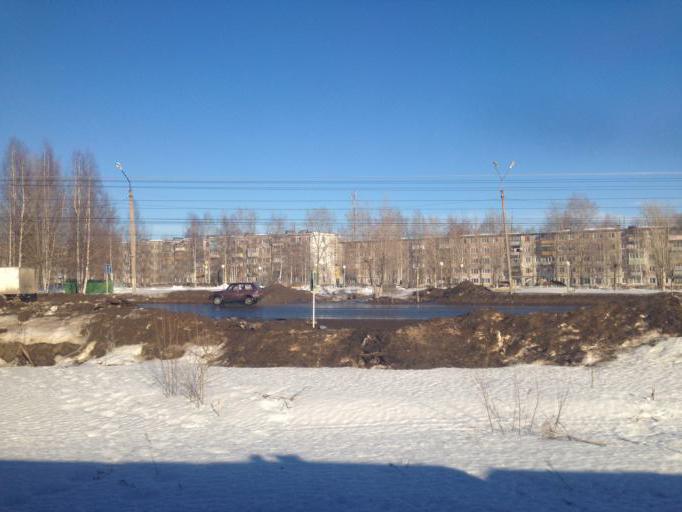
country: RU
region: Komi Republic
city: Ezhva
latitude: 61.7971
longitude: 50.7369
